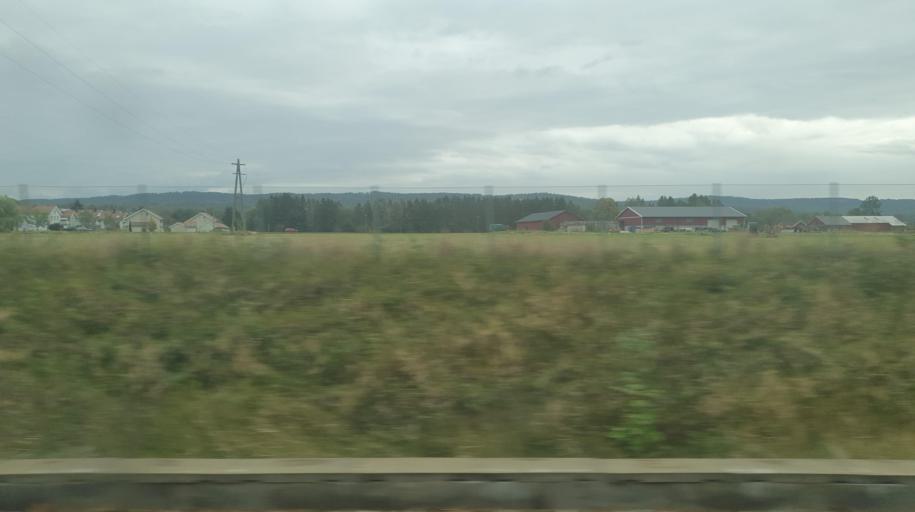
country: NO
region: Vestfold
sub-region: Sande
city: Sande
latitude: 59.5813
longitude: 10.2074
